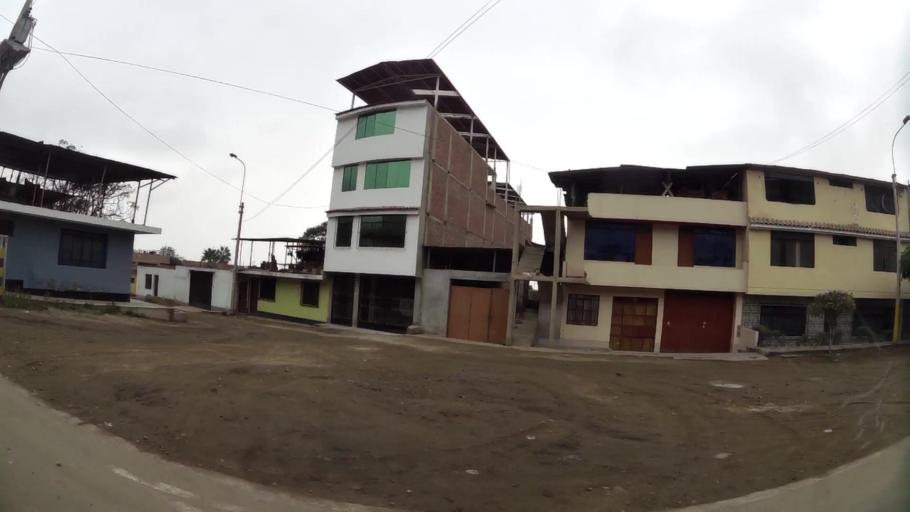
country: PE
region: Lima
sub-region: Lima
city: Surco
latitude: -12.2085
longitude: -76.9103
